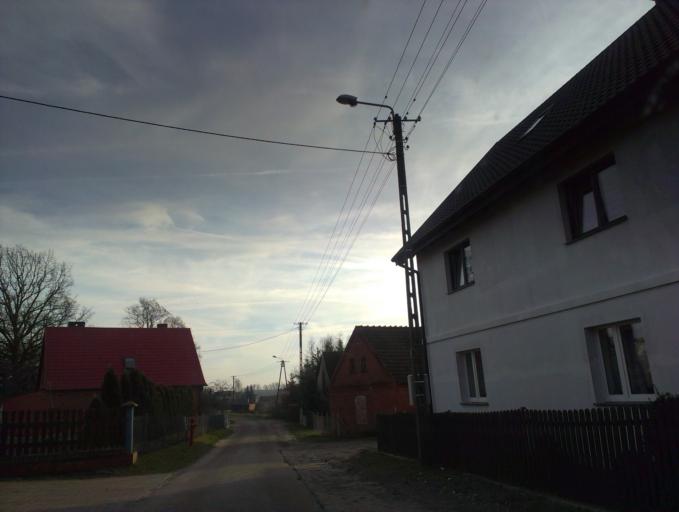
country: PL
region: Pomeranian Voivodeship
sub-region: Powiat czluchowski
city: Debrzno
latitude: 53.6161
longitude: 17.1863
